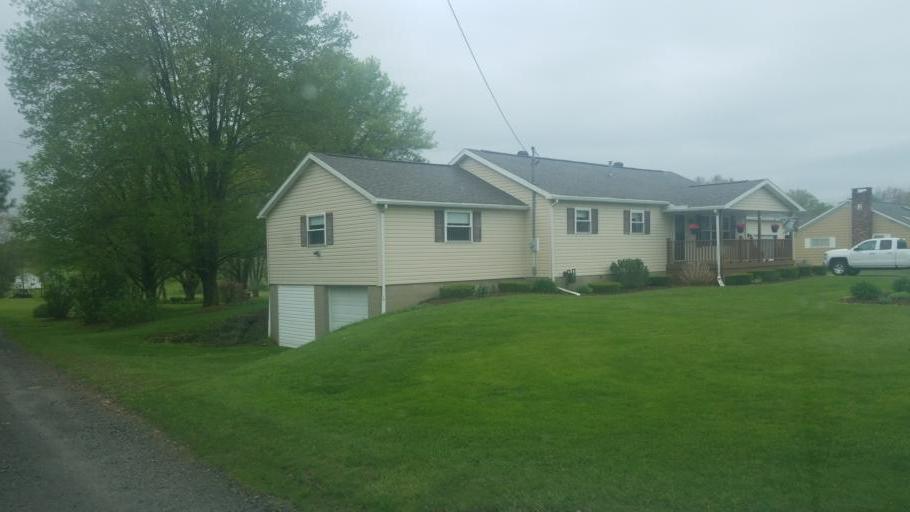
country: US
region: Pennsylvania
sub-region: Forest County
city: Tionesta
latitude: 41.3965
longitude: -79.3881
